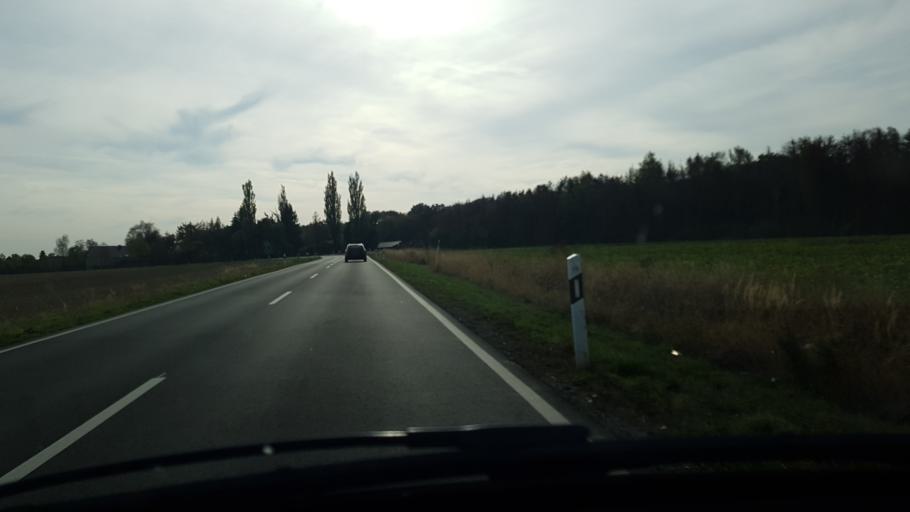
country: DE
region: Lower Saxony
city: Lehre
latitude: 52.2992
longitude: 10.6565
